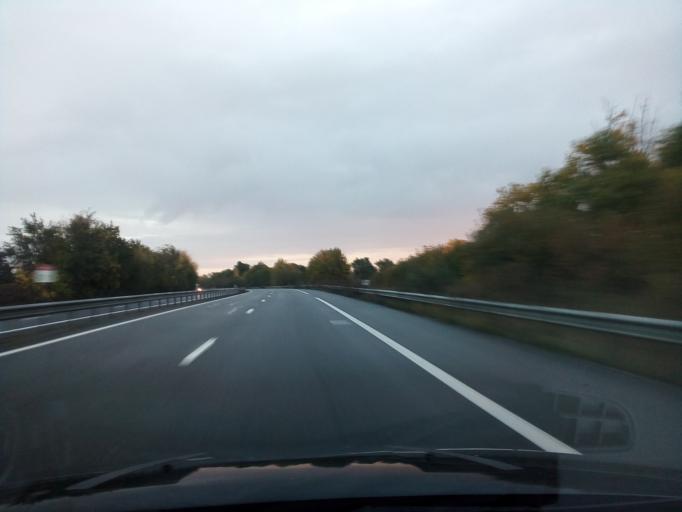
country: FR
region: Aquitaine
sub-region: Departement de la Gironde
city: Gauriaguet
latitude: 45.0605
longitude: -0.3983
